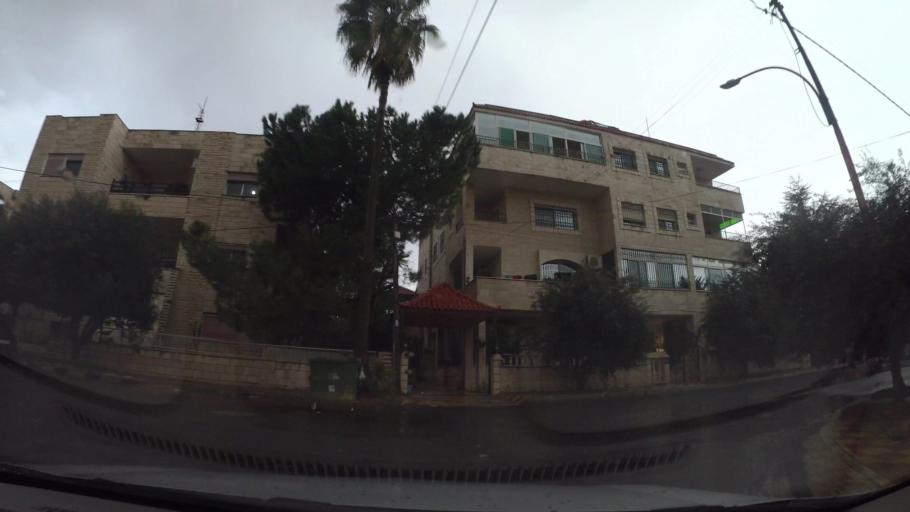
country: JO
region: Amman
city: Umm as Summaq
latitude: 31.8976
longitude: 35.8568
